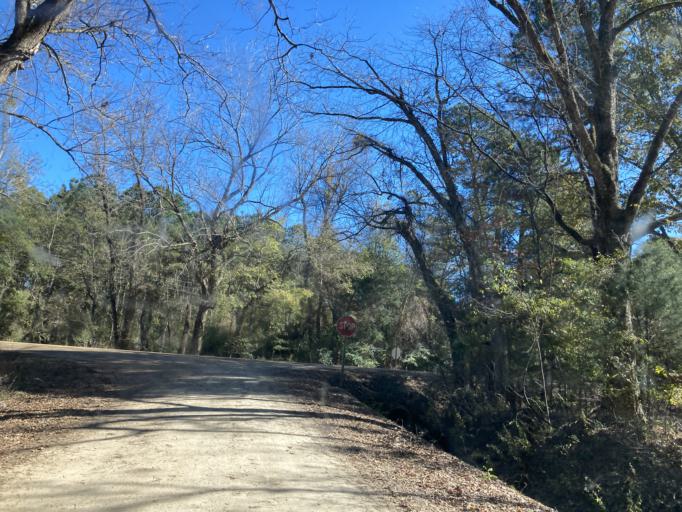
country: US
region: Mississippi
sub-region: Hinds County
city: Lynchburg
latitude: 32.5822
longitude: -90.5701
